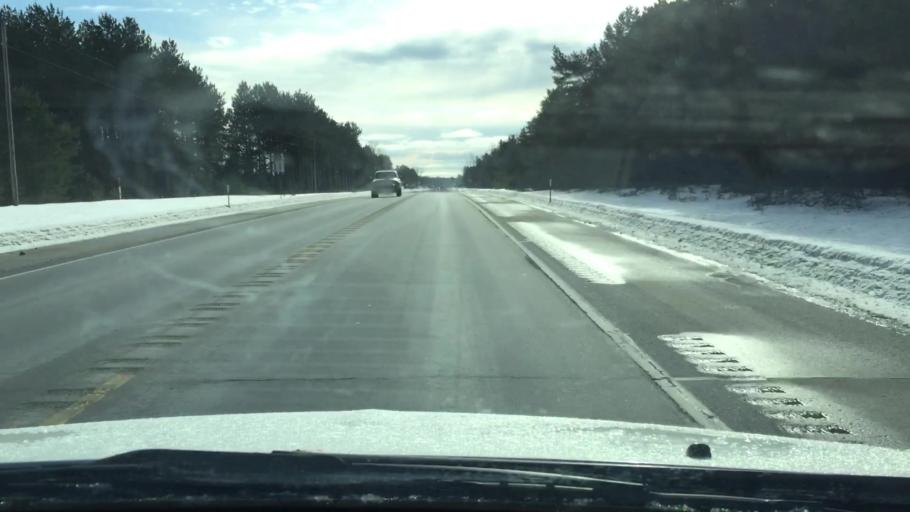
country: US
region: Michigan
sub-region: Kalkaska County
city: Kalkaska
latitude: 44.7768
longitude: -85.1585
